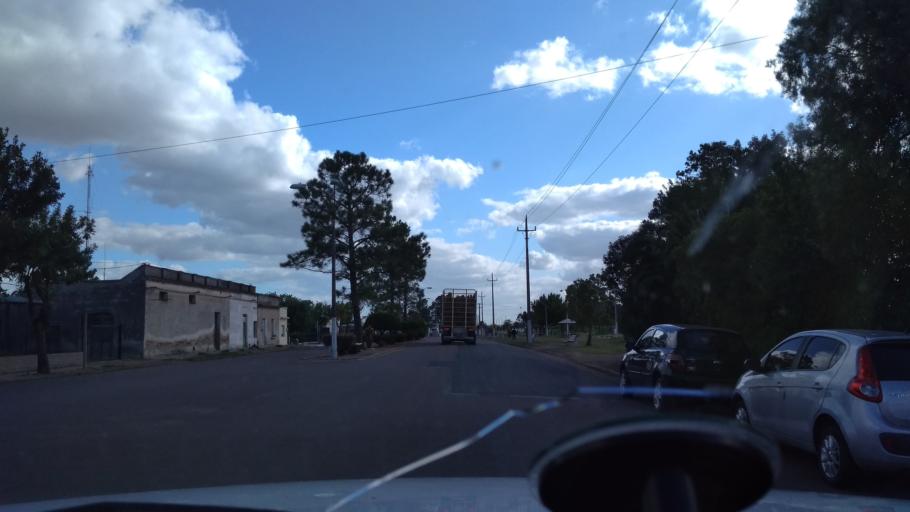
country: UY
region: Florida
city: Casupa
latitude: -34.1007
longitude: -55.6540
